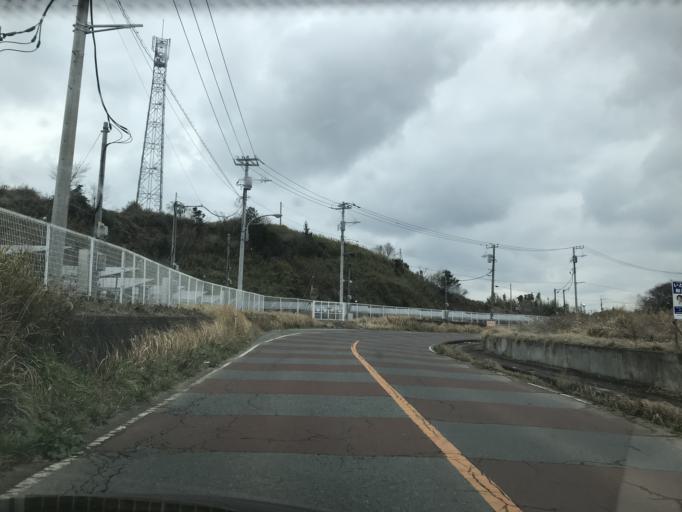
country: JP
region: Chiba
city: Sawara
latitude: 35.8350
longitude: 140.5037
